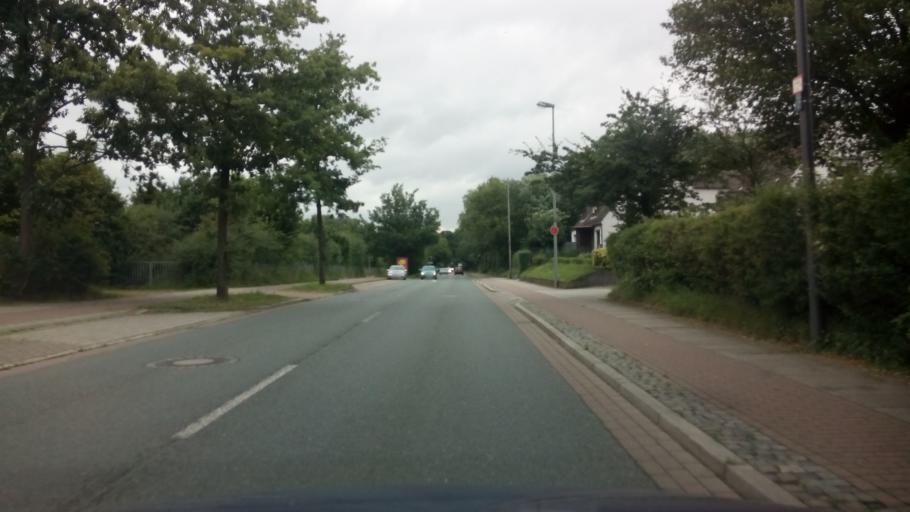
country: DE
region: Lower Saxony
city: Lemwerder
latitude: 53.1869
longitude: 8.6191
